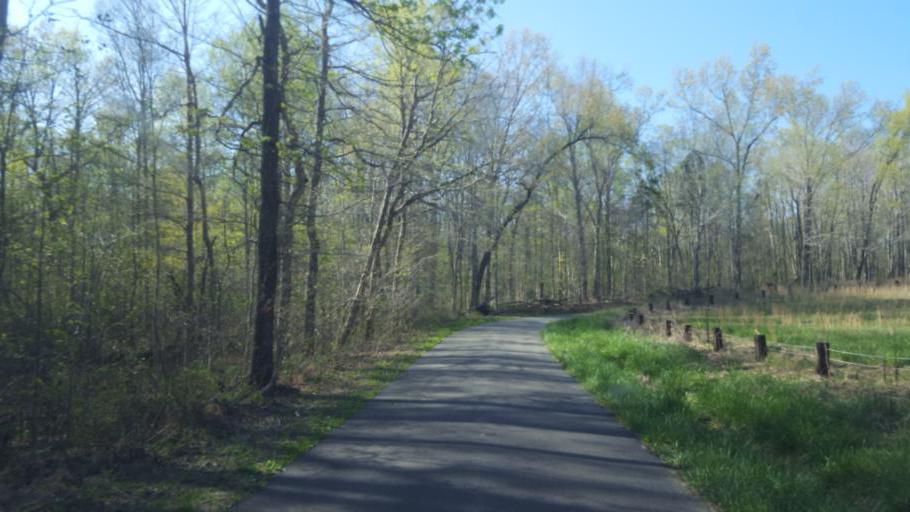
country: US
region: Kentucky
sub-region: Barren County
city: Cave City
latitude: 37.1825
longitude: -86.0490
